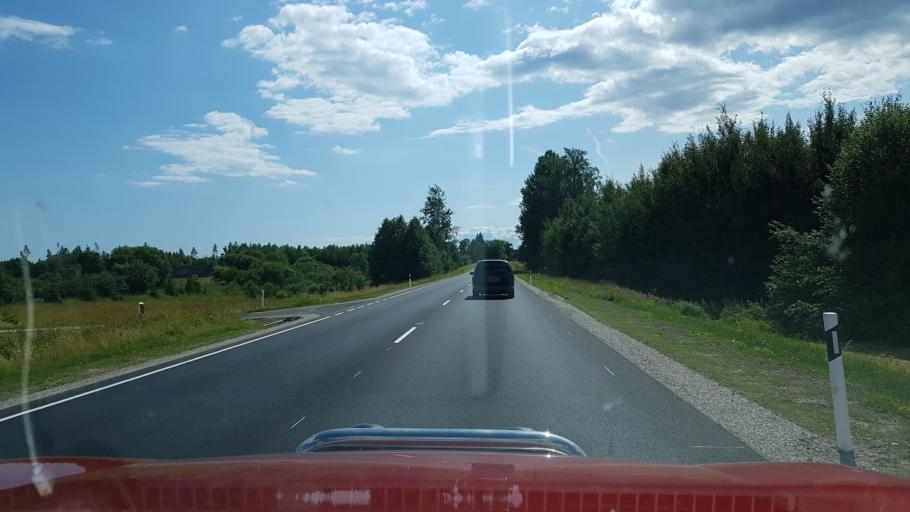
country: EE
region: Ida-Virumaa
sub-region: Johvi vald
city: Johvi
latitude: 59.0688
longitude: 27.3121
